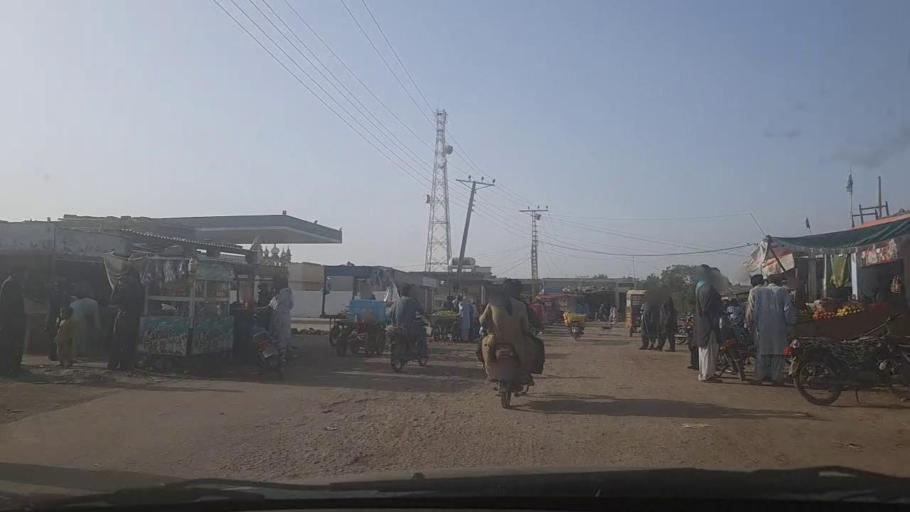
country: PK
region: Sindh
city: Keti Bandar
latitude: 24.3043
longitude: 67.6046
